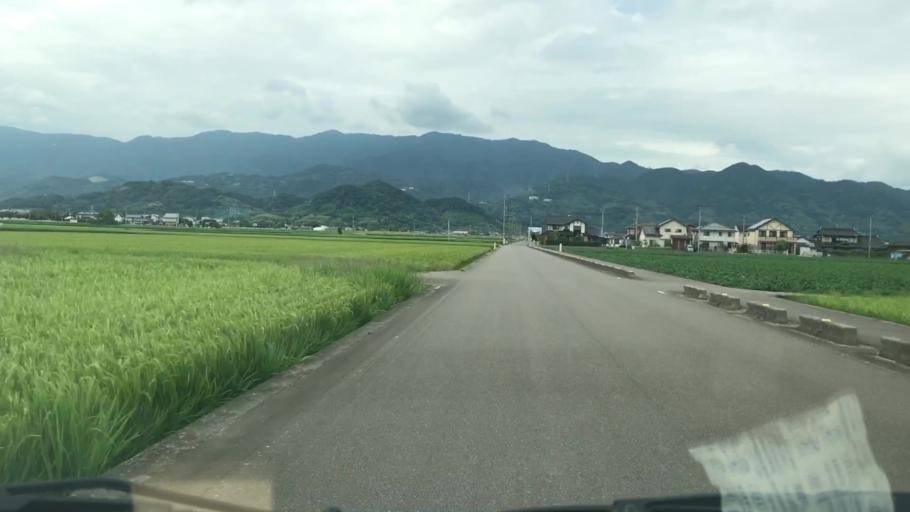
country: JP
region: Saga Prefecture
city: Saga-shi
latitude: 33.2837
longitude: 130.2259
